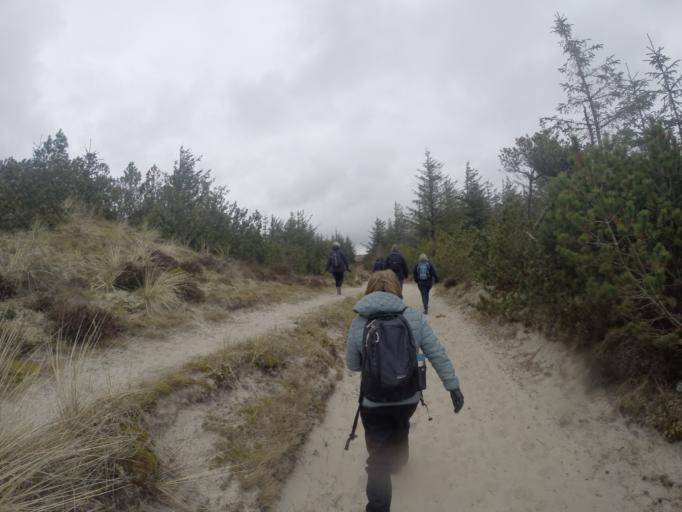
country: DK
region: North Denmark
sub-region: Thisted Kommune
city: Hurup
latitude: 56.8999
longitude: 8.3385
